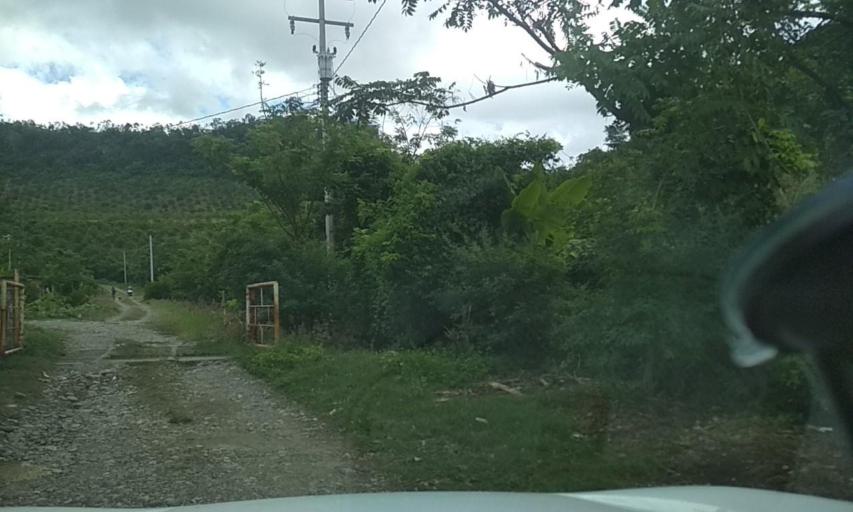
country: MX
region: Veracruz
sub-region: Papantla
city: Polutla
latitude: 20.5436
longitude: -97.2515
